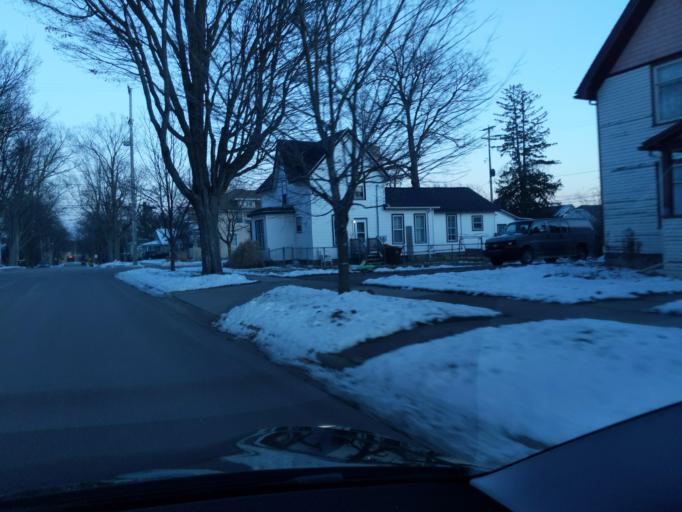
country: US
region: Michigan
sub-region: Ingham County
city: Mason
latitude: 42.5772
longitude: -84.4404
